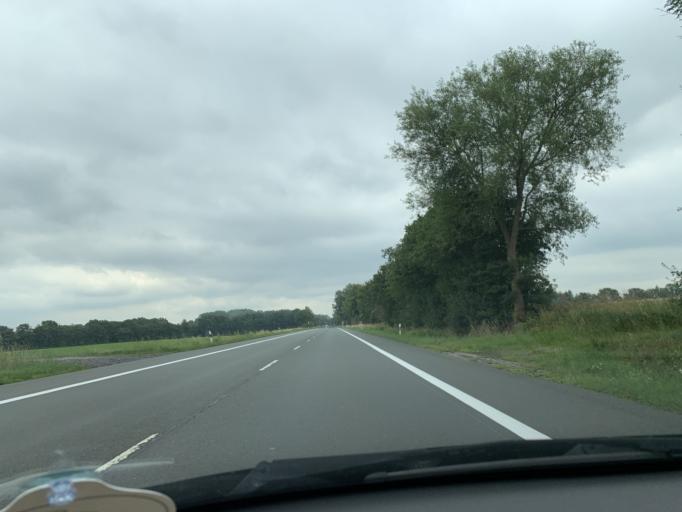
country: DE
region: North Rhine-Westphalia
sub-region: Regierungsbezirk Munster
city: Warendorf
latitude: 51.9099
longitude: 8.0466
